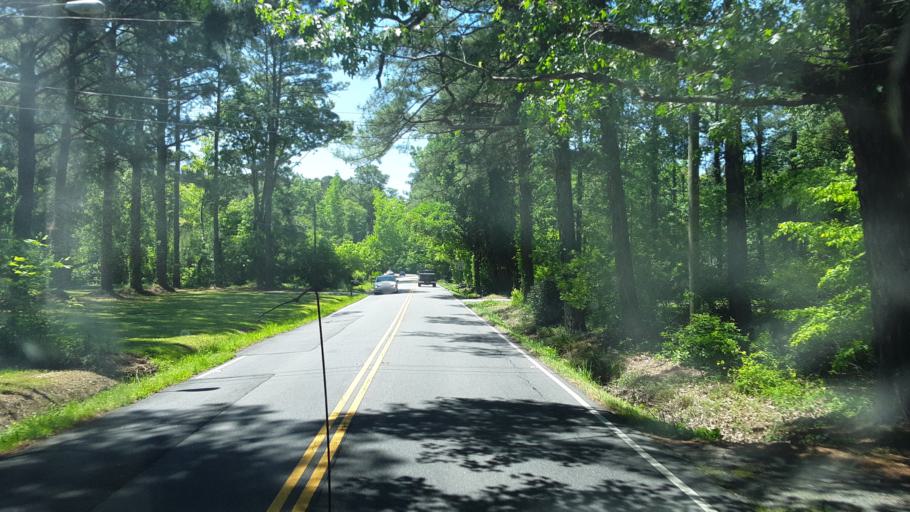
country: US
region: Virginia
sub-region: City of Virginia Beach
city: Virginia Beach
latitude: 36.7372
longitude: -75.9892
